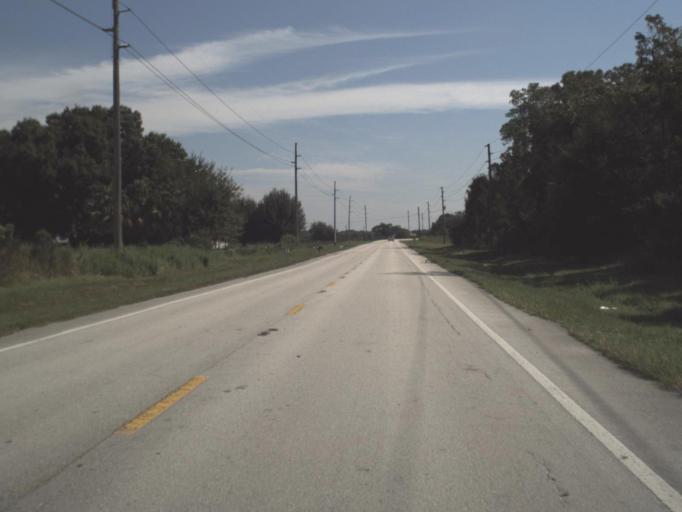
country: US
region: Florida
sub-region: Hardee County
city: Wauchula
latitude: 27.5606
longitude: -81.6653
